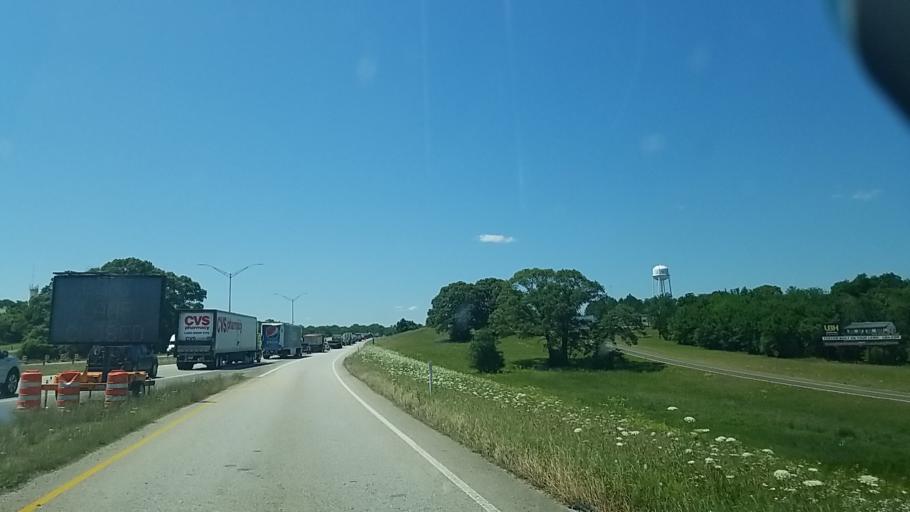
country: US
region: Texas
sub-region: Leon County
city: Buffalo
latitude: 31.4540
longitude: -96.0784
